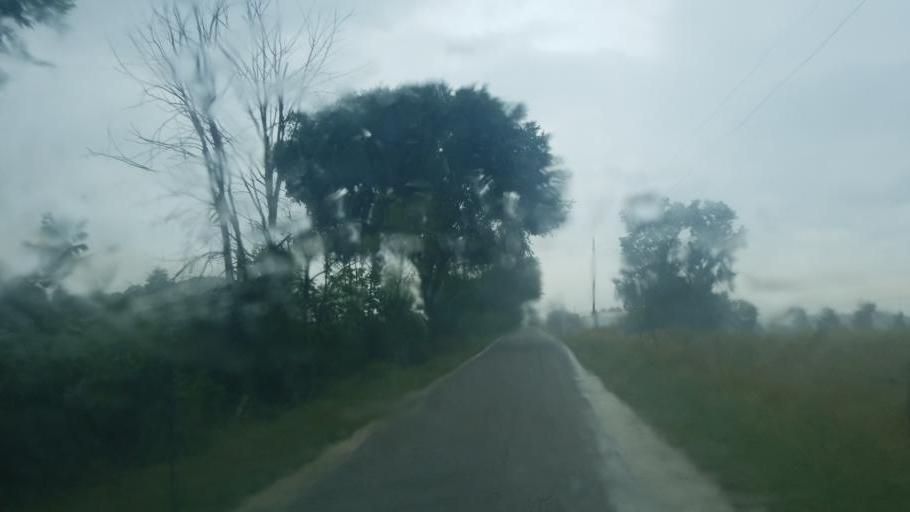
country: US
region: Indiana
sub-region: DeKalb County
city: Butler
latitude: 41.4639
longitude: -84.8304
